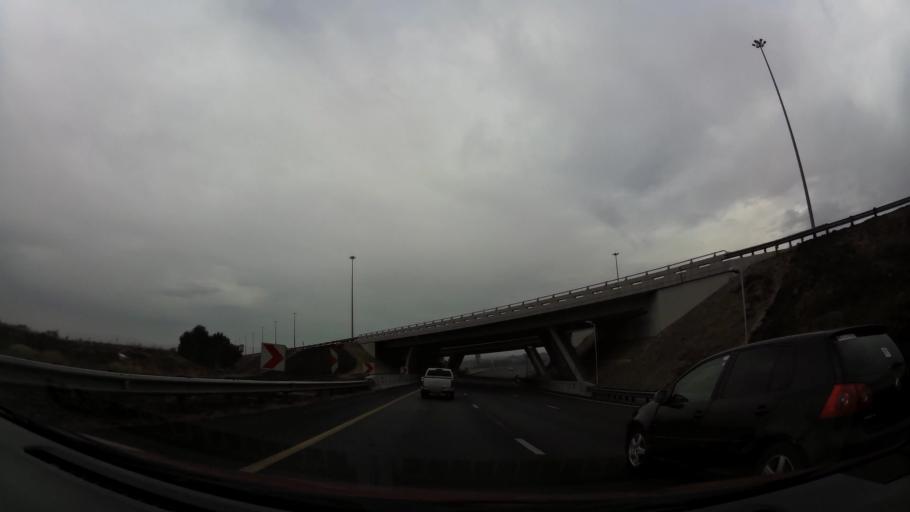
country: ZA
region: Gauteng
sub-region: City of Johannesburg Metropolitan Municipality
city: Soweto
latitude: -26.3045
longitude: 27.9455
